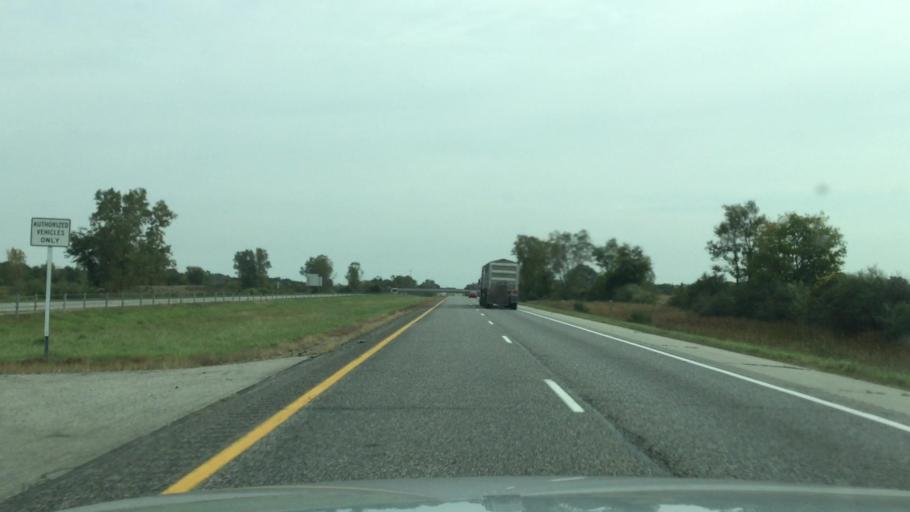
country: US
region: Michigan
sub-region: Shiawassee County
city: Corunna
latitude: 42.9006
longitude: -84.0762
